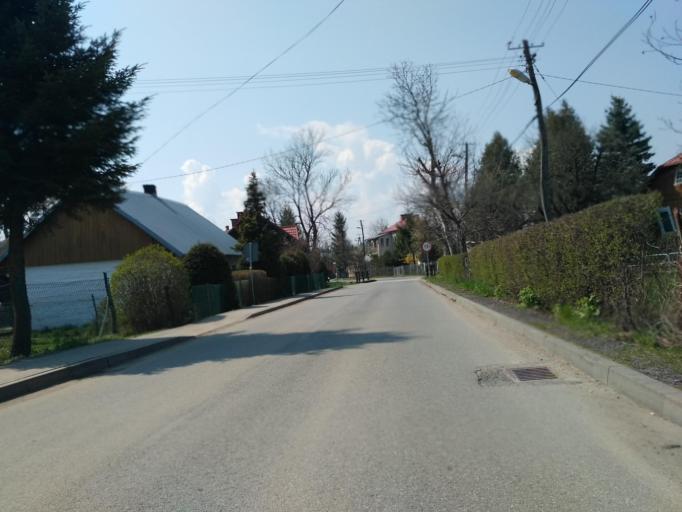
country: PL
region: Subcarpathian Voivodeship
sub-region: Powiat sanocki
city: Zarszyn
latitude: 49.5797
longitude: 22.0127
